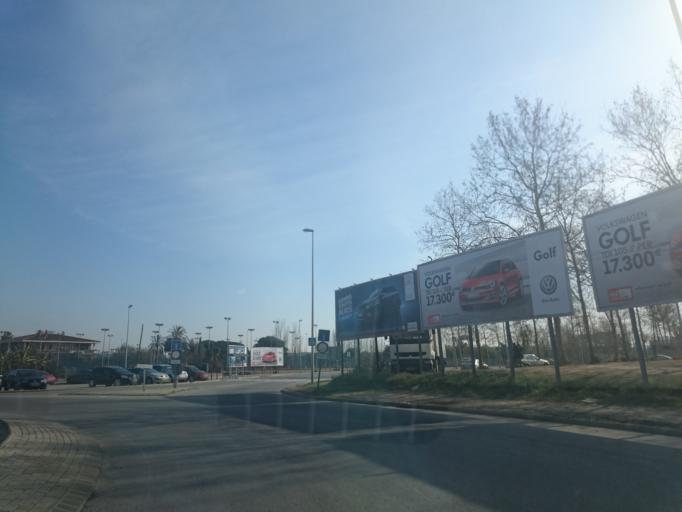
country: ES
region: Catalonia
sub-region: Provincia de Barcelona
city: L'Hospitalet de Llobregat
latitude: 41.3433
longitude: 2.1103
